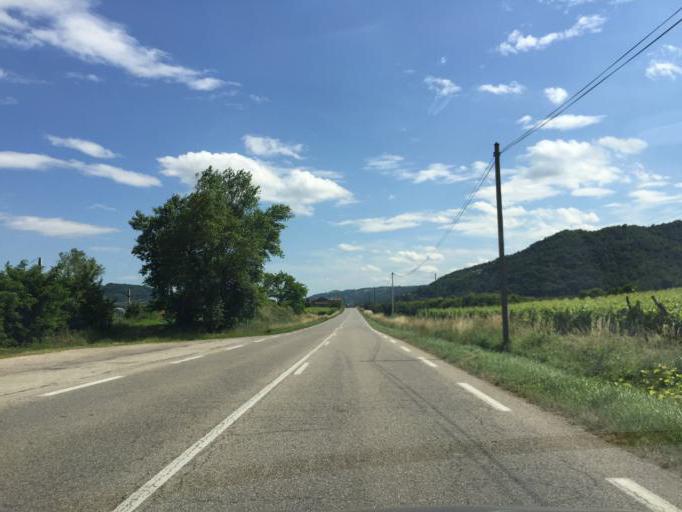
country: FR
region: Rhone-Alpes
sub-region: Departement de l'Ardeche
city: Andance
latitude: 45.2214
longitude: 4.8033
